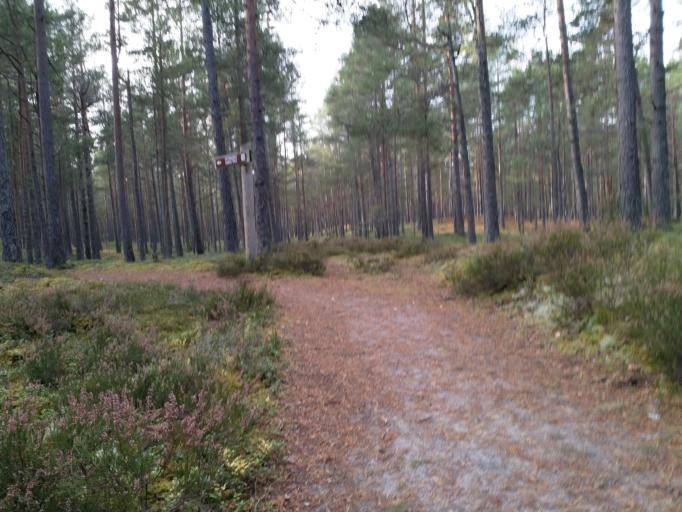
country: LV
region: Dundaga
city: Dundaga
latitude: 57.6513
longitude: 22.2664
